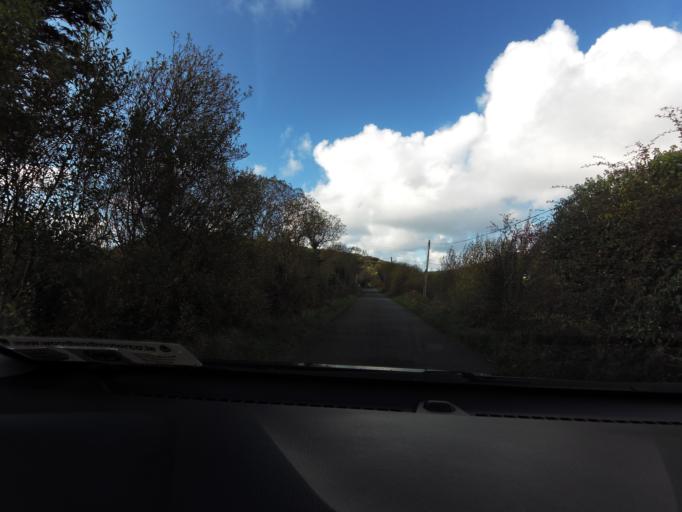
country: IE
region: Connaught
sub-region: Maigh Eo
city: Westport
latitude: 53.7736
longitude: -9.7705
